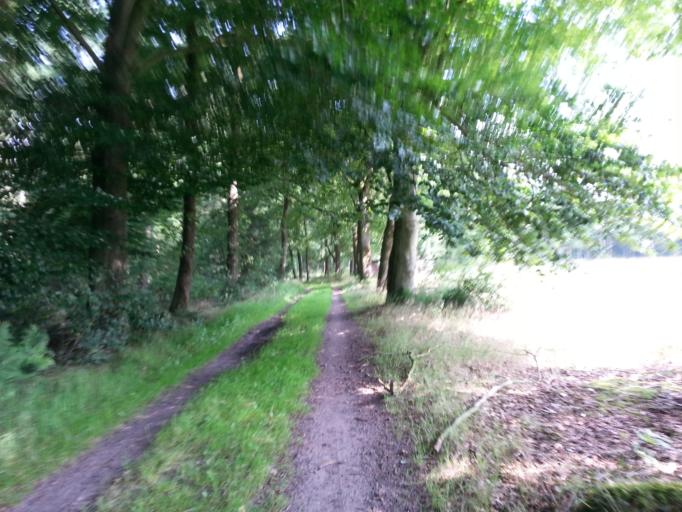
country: NL
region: Utrecht
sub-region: Gemeente Utrechtse Heuvelrug
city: Maarn
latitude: 52.0912
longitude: 5.3846
